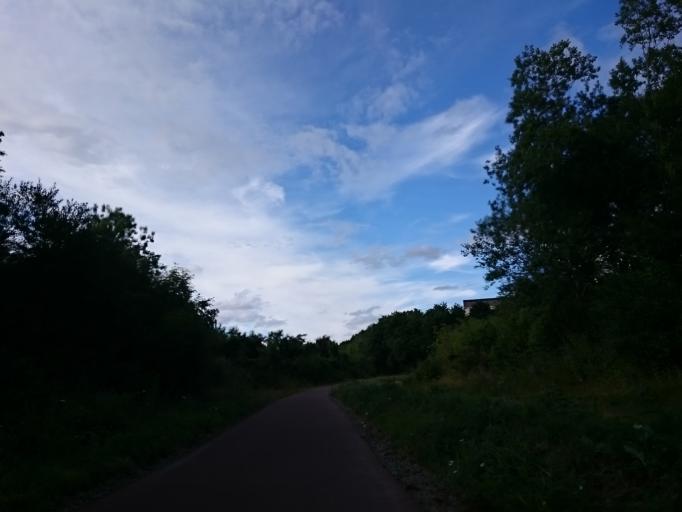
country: FR
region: Lower Normandy
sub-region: Departement du Calvados
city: May-sur-Orne
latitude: 49.1034
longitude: -0.3855
